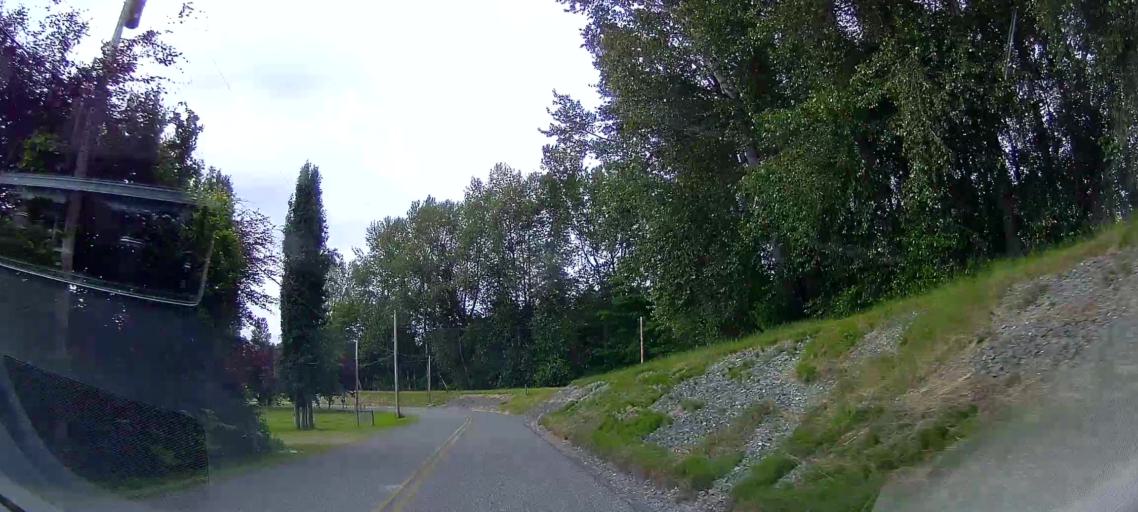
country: US
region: Washington
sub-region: Skagit County
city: Mount Vernon
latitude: 48.3466
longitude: -122.3573
